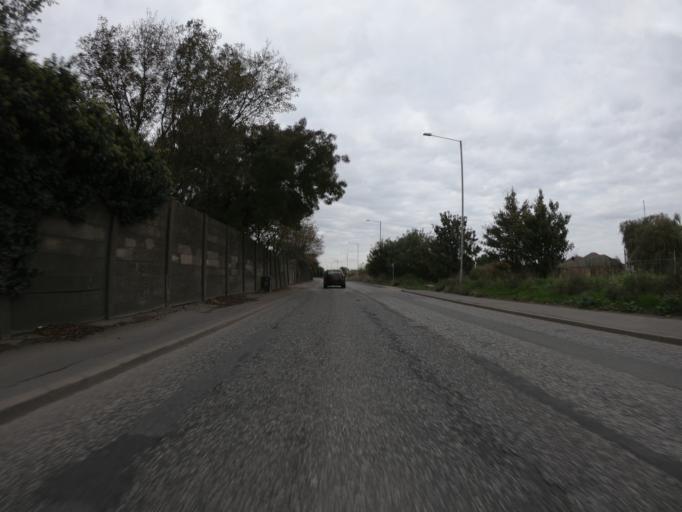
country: GB
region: England
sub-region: Borough of Thurrock
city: Tilbury
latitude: 51.4591
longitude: 0.3590
